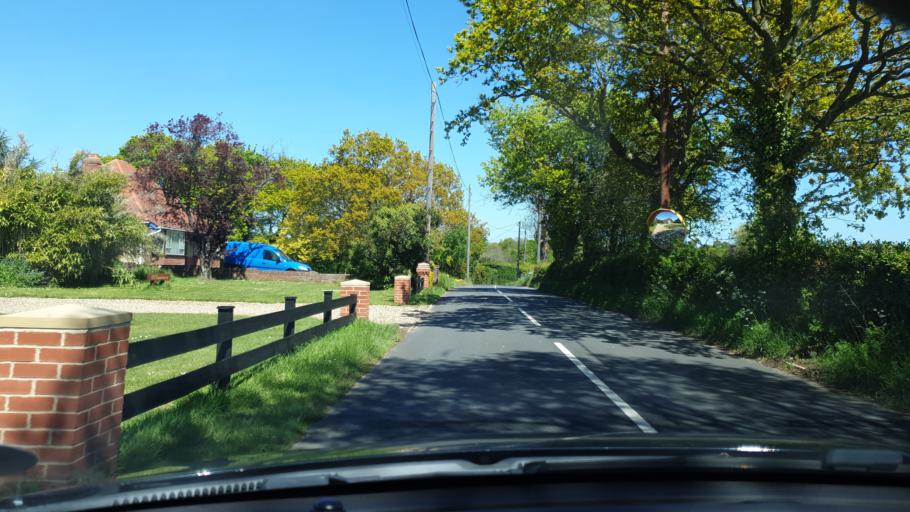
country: GB
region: England
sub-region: Essex
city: Little Clacton
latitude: 51.8641
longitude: 1.1206
